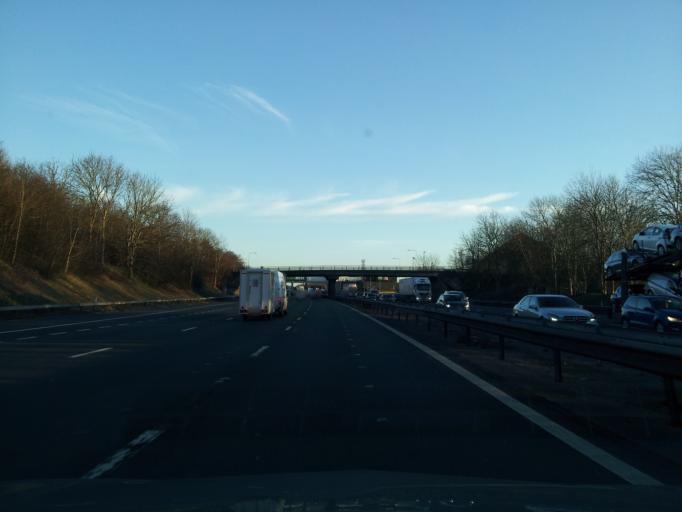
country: GB
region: England
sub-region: Milton Keynes
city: Newport Pagnell
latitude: 52.0856
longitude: -0.7513
